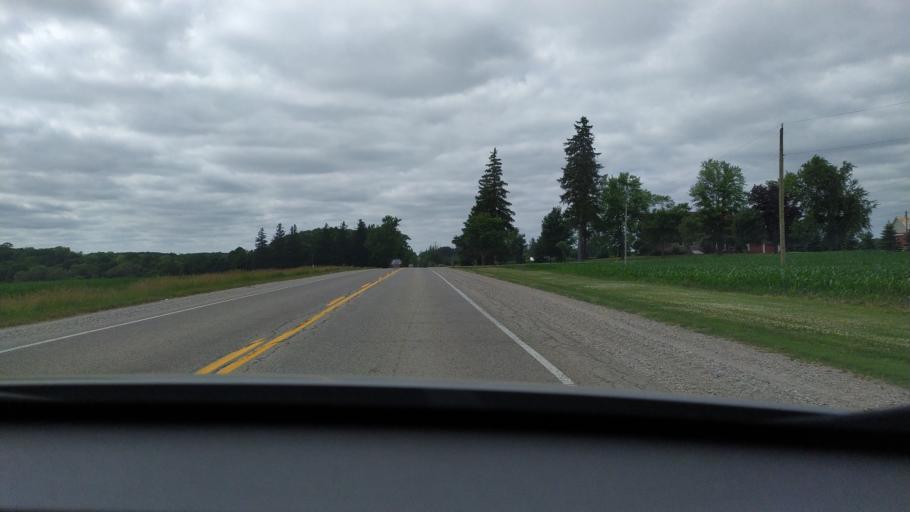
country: CA
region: Ontario
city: Stratford
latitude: 43.2899
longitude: -80.9697
